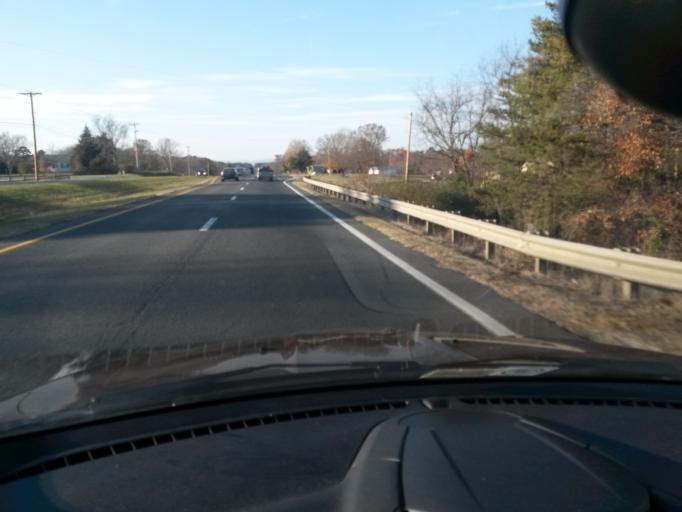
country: US
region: Virginia
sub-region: Campbell County
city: Concord
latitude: 37.3635
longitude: -79.0083
